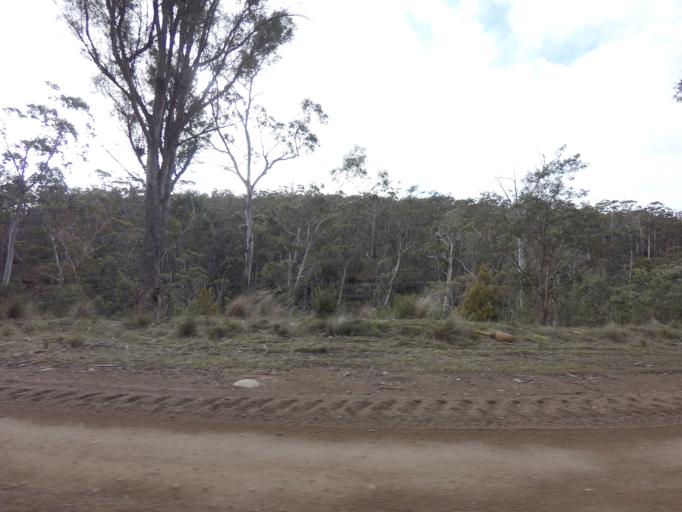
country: AU
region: Tasmania
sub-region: Derwent Valley
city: New Norfolk
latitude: -42.7482
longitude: 146.8690
